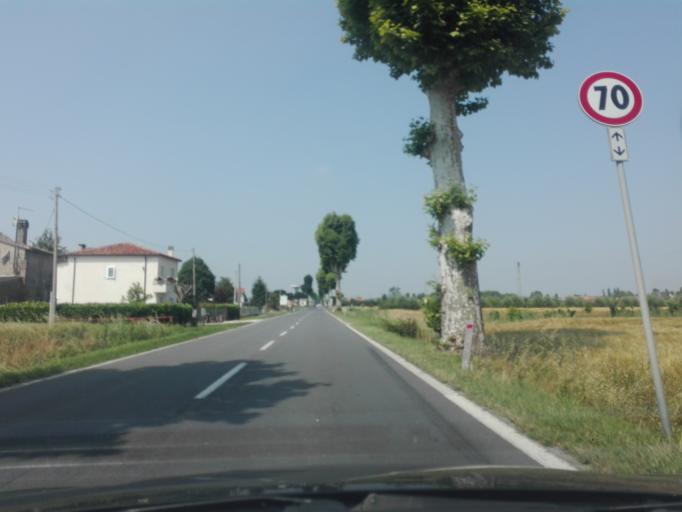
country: IT
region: Veneto
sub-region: Provincia di Rovigo
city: Villadose
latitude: 45.0647
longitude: 11.9149
